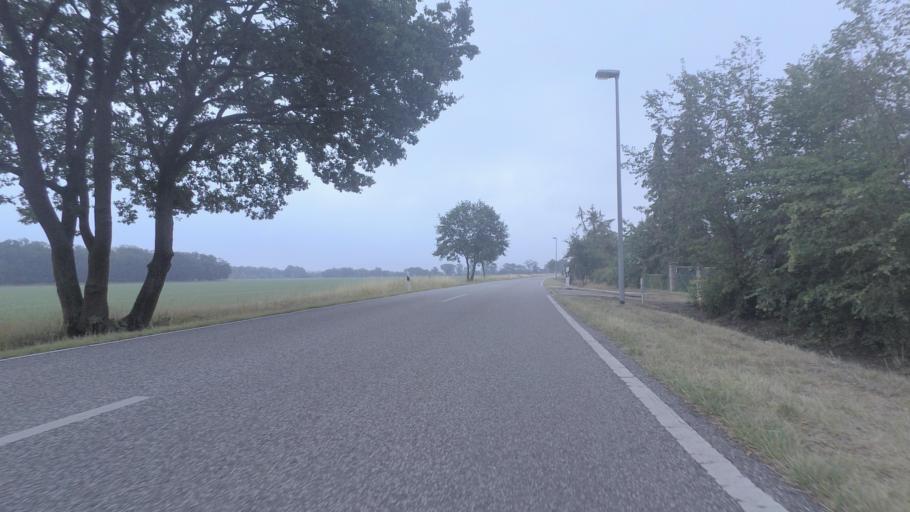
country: DE
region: Brandenburg
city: Paulinenaue
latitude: 52.6675
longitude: 12.7225
